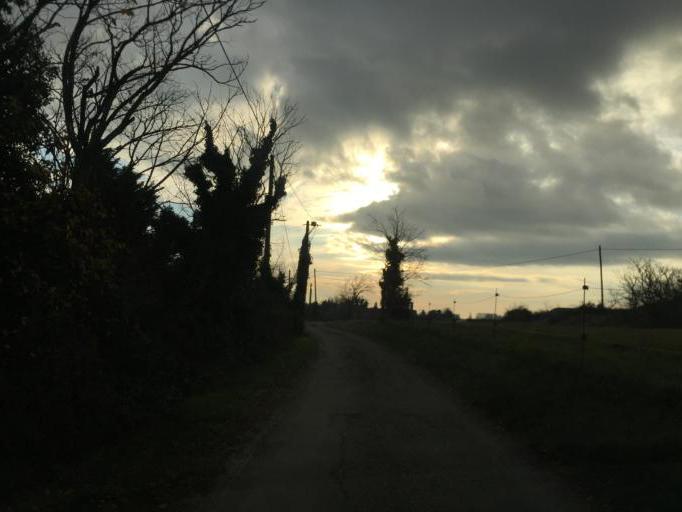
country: FR
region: Provence-Alpes-Cote d'Azur
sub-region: Departement du Vaucluse
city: Courthezon
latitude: 44.1092
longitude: 4.8763
